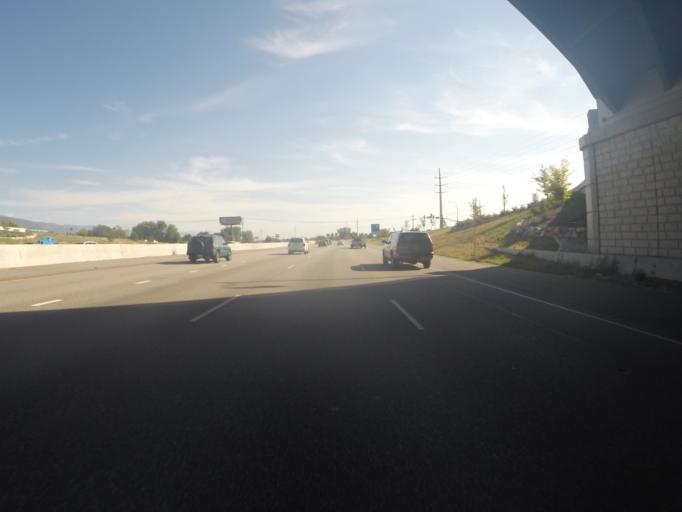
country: US
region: Utah
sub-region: Davis County
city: Layton
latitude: 41.0560
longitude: -111.9611
